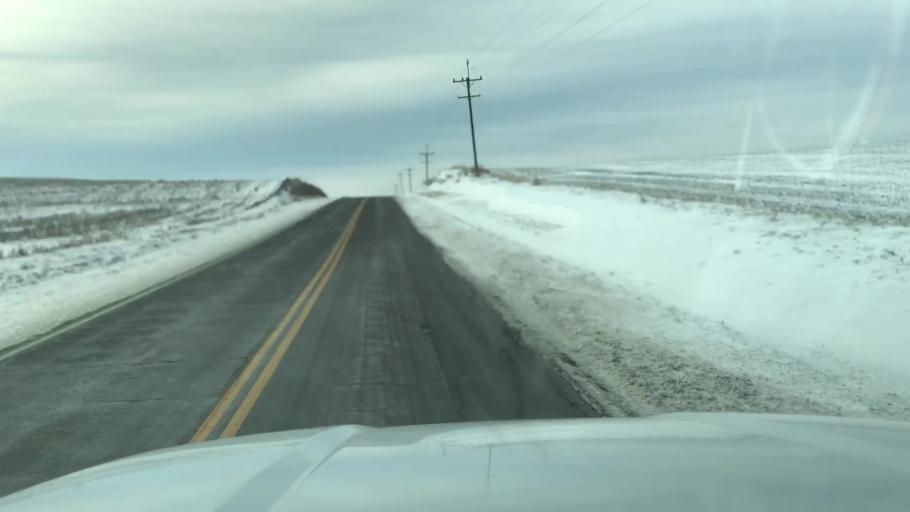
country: US
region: Missouri
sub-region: Holt County
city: Mound City
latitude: 40.1069
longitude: -95.1449
